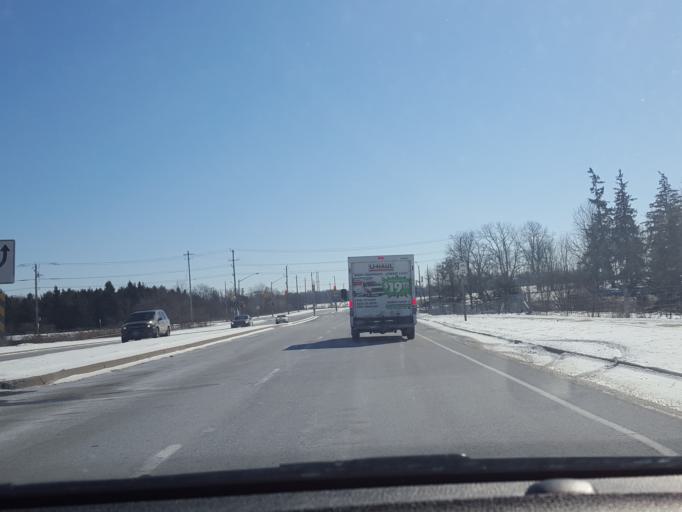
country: CA
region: Ontario
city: Waterloo
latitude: 43.4851
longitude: -80.5668
